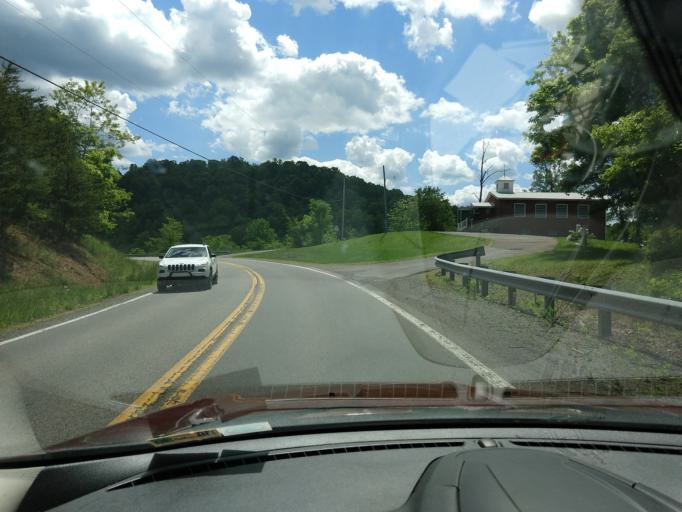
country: US
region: West Virginia
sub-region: Gilmer County
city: Glenville
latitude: 38.9302
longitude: -80.7912
